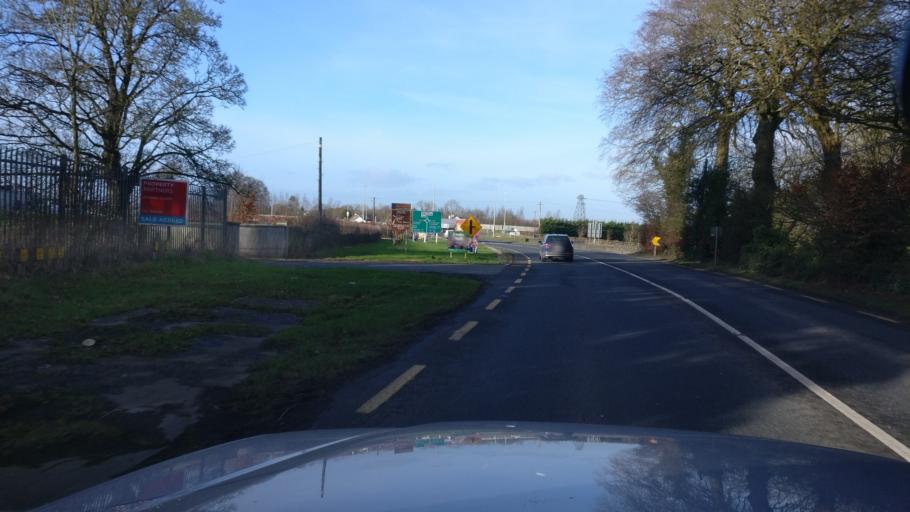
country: IE
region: Leinster
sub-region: Uibh Fhaili
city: Tullamore
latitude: 53.2523
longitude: -7.4773
